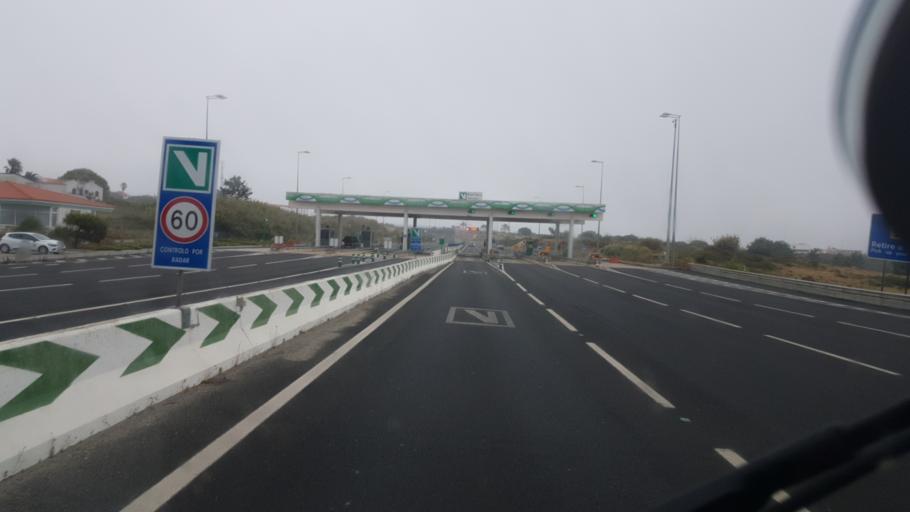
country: PT
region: Lisbon
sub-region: Mafra
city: Ericeira
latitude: 38.9638
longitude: -9.4045
